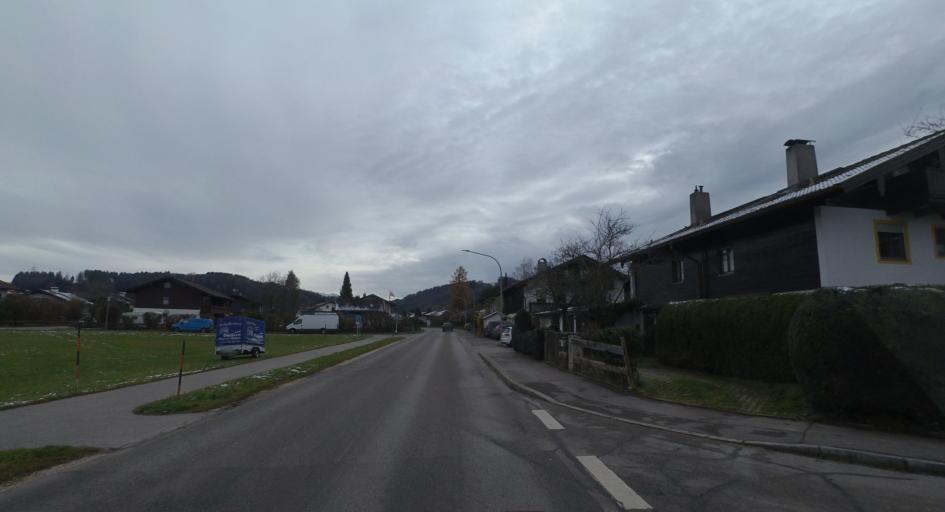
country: DE
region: Bavaria
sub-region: Upper Bavaria
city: Vachendorf
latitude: 47.8458
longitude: 12.6037
